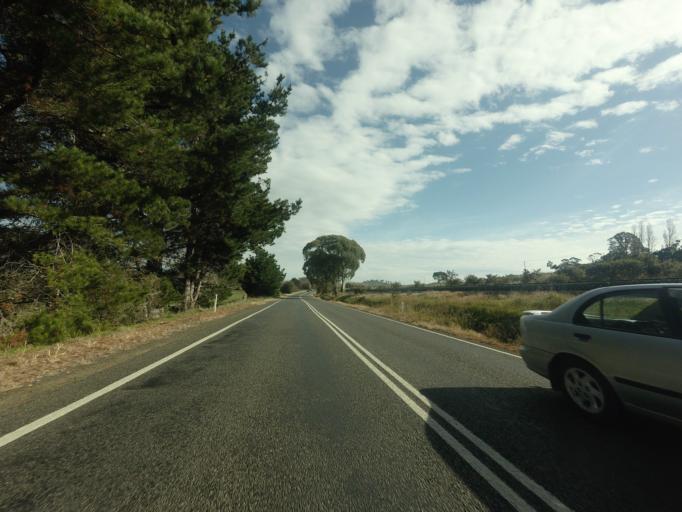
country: AU
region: Tasmania
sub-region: Meander Valley
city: Westbury
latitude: -41.5269
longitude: 146.8145
